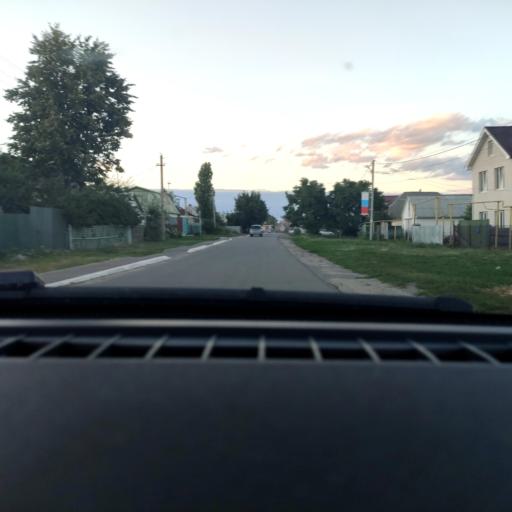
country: RU
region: Voronezj
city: Novaya Usman'
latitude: 51.6575
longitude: 39.3385
